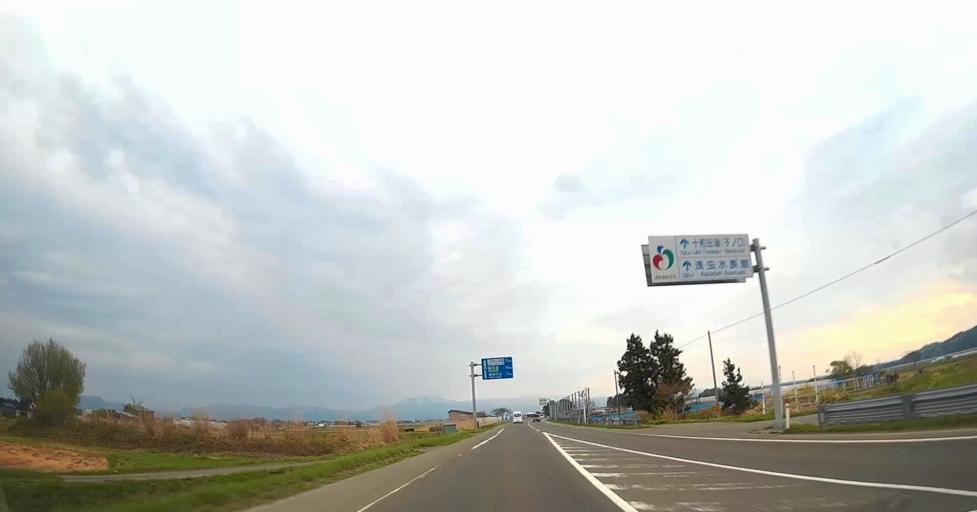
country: JP
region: Aomori
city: Aomori Shi
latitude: 40.9023
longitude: 140.6660
